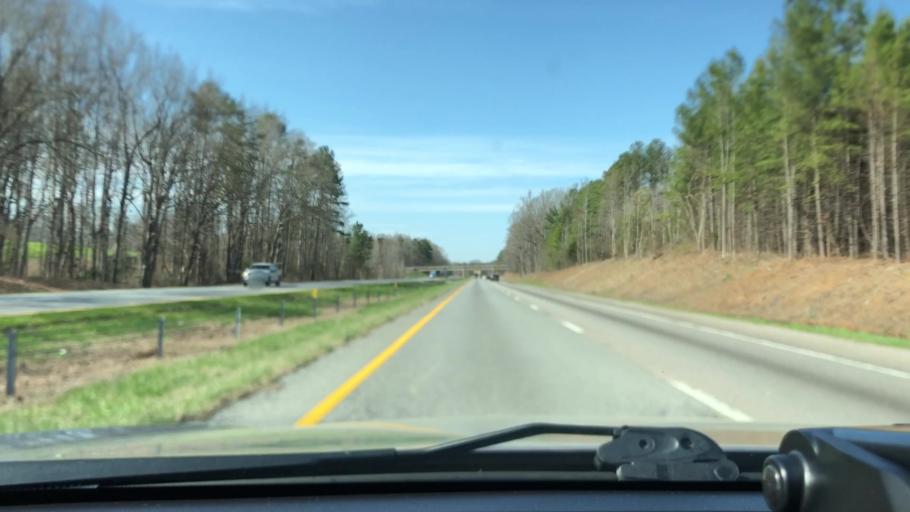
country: US
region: South Carolina
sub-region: Spartanburg County
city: Roebuck
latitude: 34.8738
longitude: -81.9893
